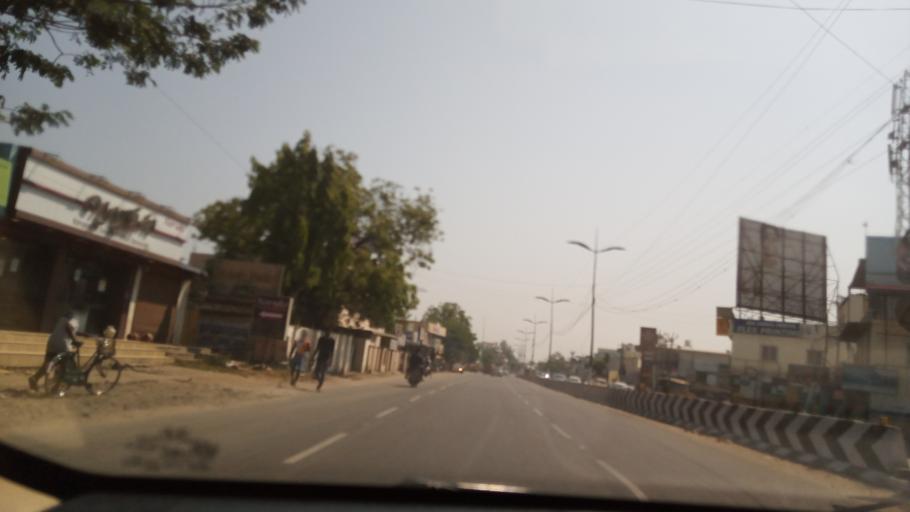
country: IN
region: Tamil Nadu
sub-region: Coimbatore
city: Irugur
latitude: 11.0440
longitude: 77.0465
